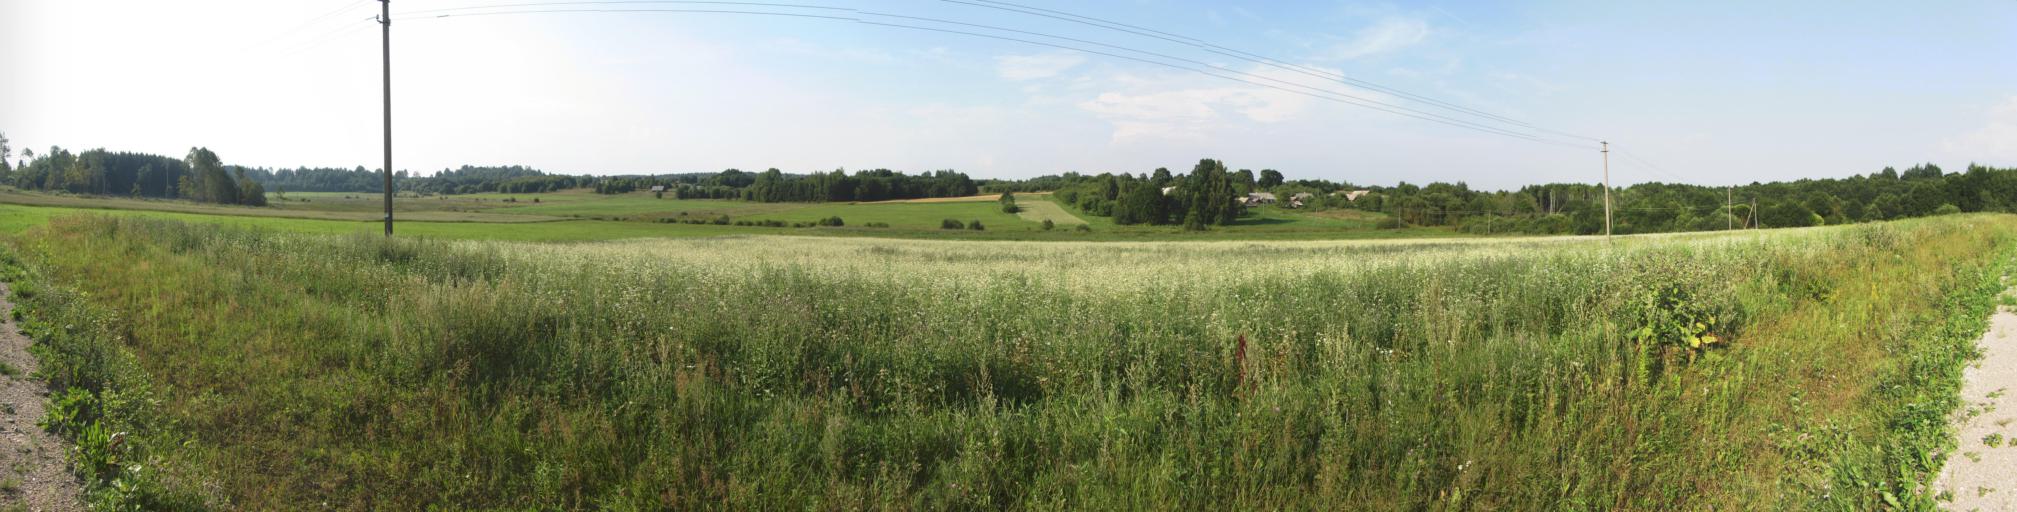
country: LT
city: Skaidiskes
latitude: 54.4969
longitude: 25.5843
